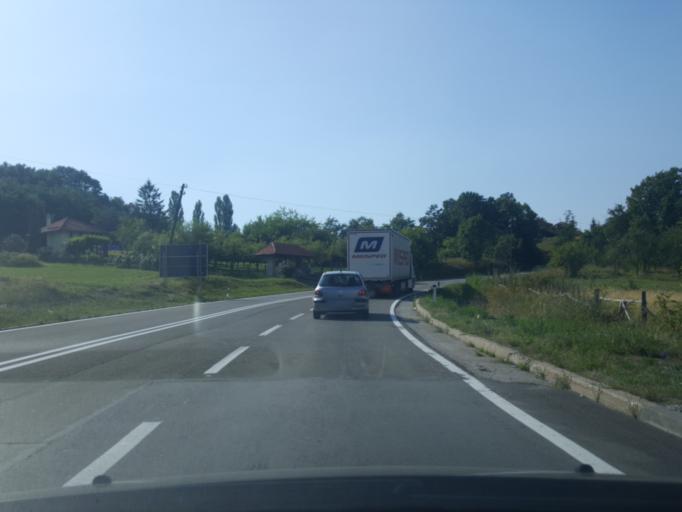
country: RS
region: Central Serbia
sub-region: Moravicki Okrug
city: Gornji Milanovac
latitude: 44.1172
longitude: 20.4836
